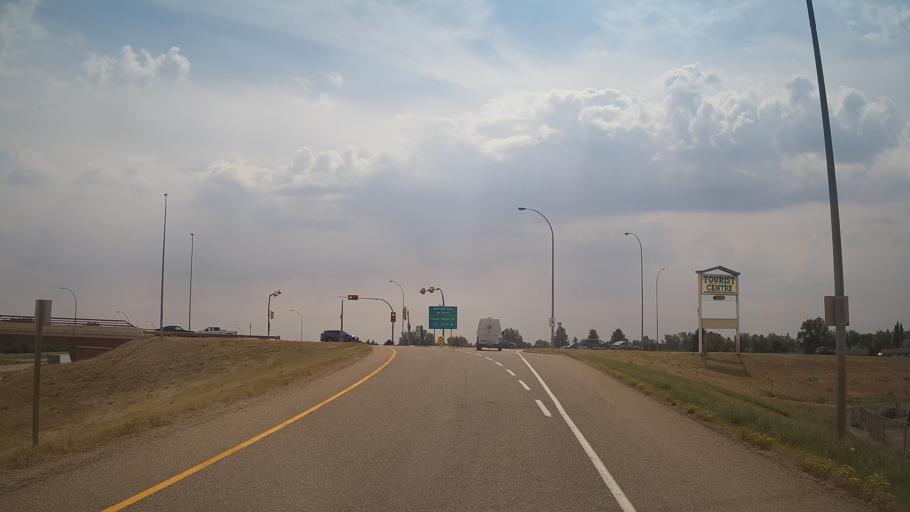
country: CA
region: Alberta
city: Medicine Hat
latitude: 50.0122
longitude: -110.6840
